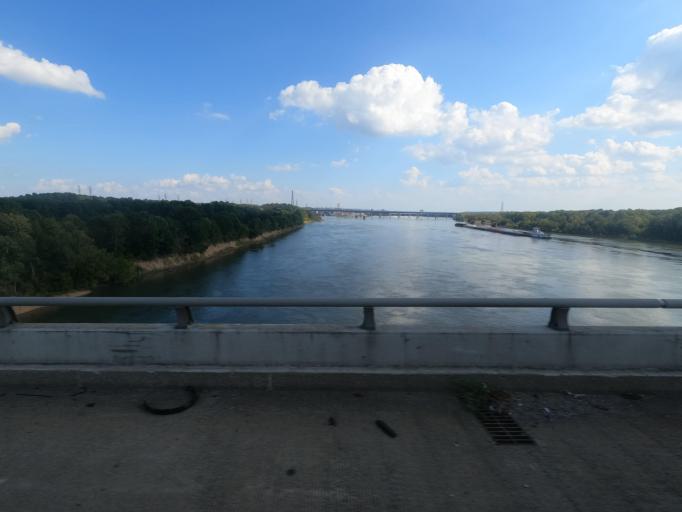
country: US
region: Kentucky
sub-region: Marshall County
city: Calvert City
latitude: 37.0271
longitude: -88.2843
